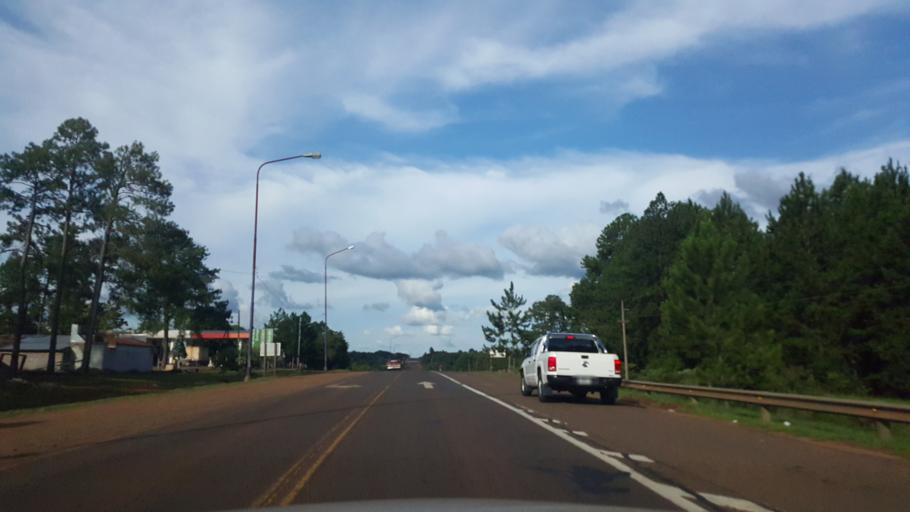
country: AR
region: Misiones
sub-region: Departamento de San Ignacio
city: San Ignacio
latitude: -27.2674
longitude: -55.5387
